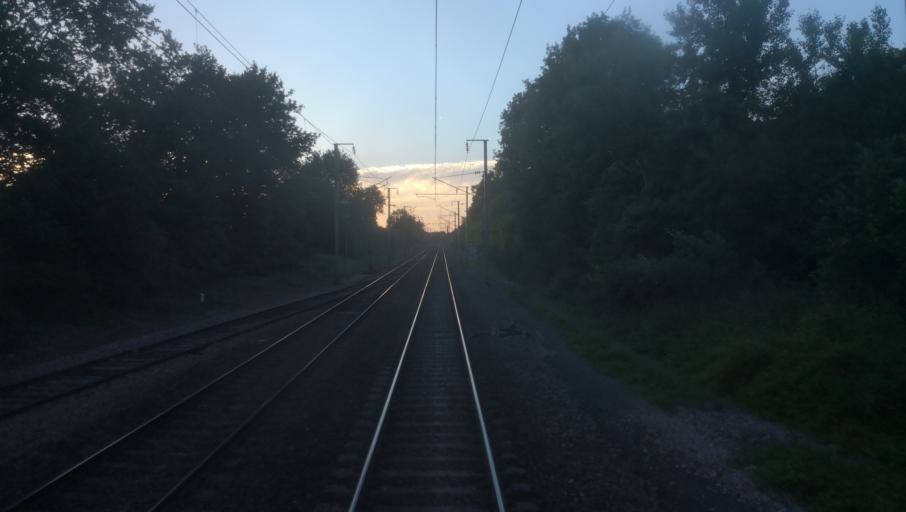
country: FR
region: Haute-Normandie
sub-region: Departement de l'Eure
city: Evreux
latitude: 48.9992
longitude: 1.2099
